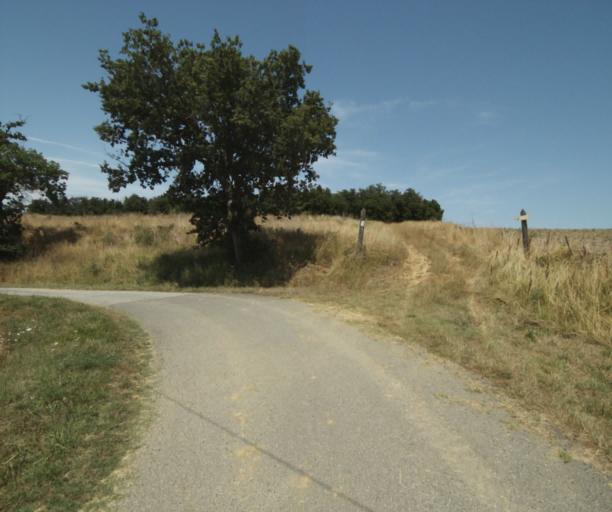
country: FR
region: Midi-Pyrenees
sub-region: Departement de la Haute-Garonne
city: Saint-Felix-Lauragais
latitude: 43.4537
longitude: 1.8506
